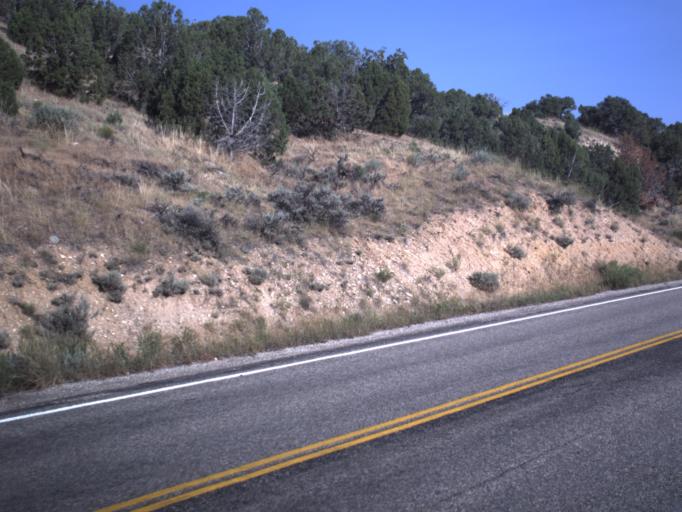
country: US
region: Utah
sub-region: Uintah County
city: Vernal
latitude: 40.6025
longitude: -109.4666
